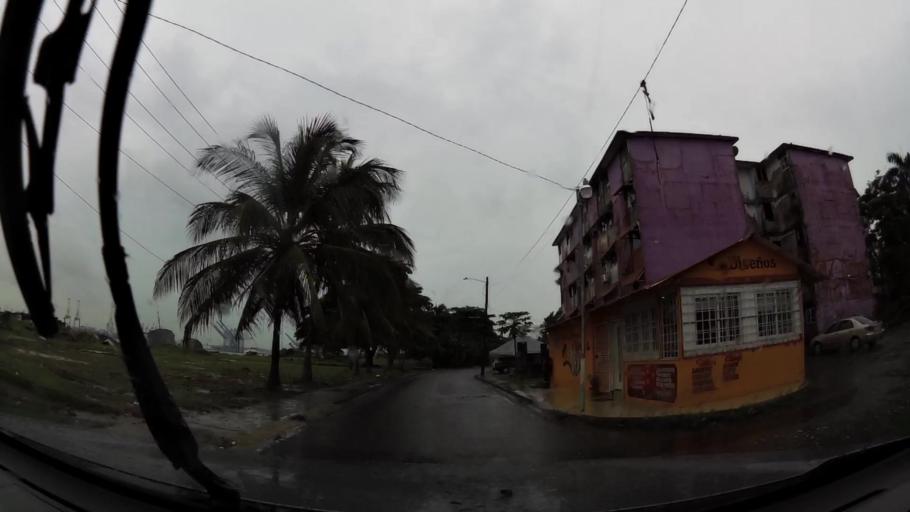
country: PA
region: Colon
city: Colon
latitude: 9.3663
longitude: -79.9007
